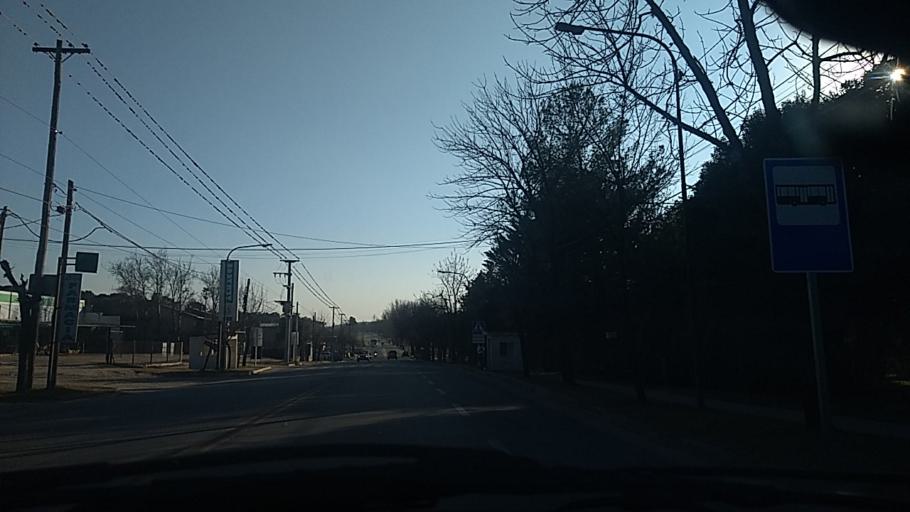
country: AR
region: Cordoba
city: Salsipuedes
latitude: -31.1310
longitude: -64.2953
